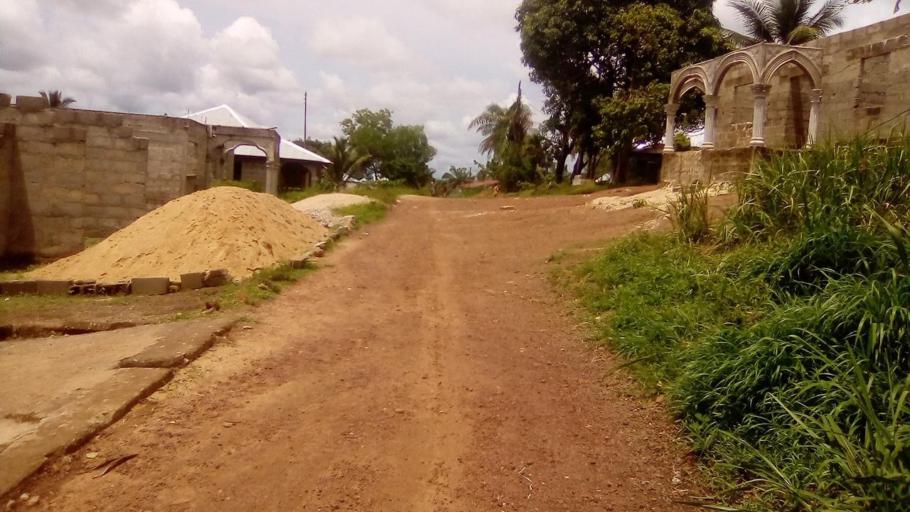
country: SL
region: Southern Province
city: Bo
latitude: 7.9391
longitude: -11.7353
